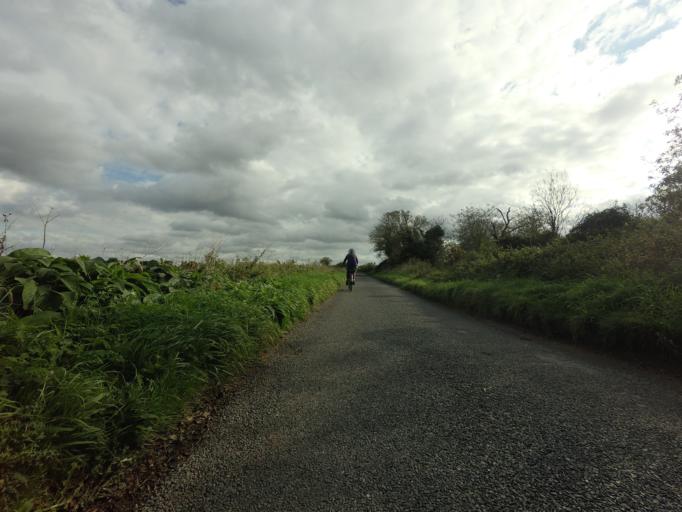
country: GB
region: England
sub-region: Norfolk
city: Dersingham
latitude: 52.8602
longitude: 0.5129
